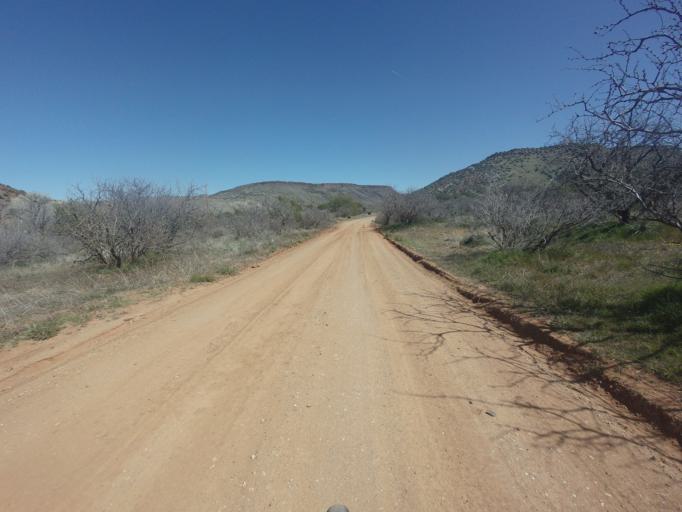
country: US
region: Arizona
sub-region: Yavapai County
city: Lake Montezuma
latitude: 34.6663
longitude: -111.7154
